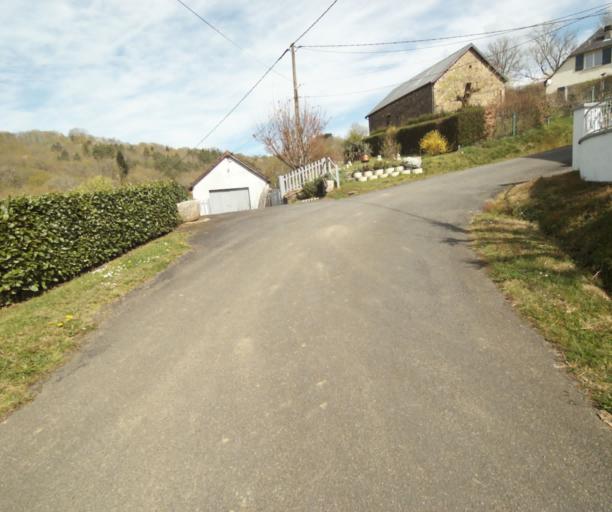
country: FR
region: Limousin
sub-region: Departement de la Correze
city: Laguenne
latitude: 45.2471
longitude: 1.8115
